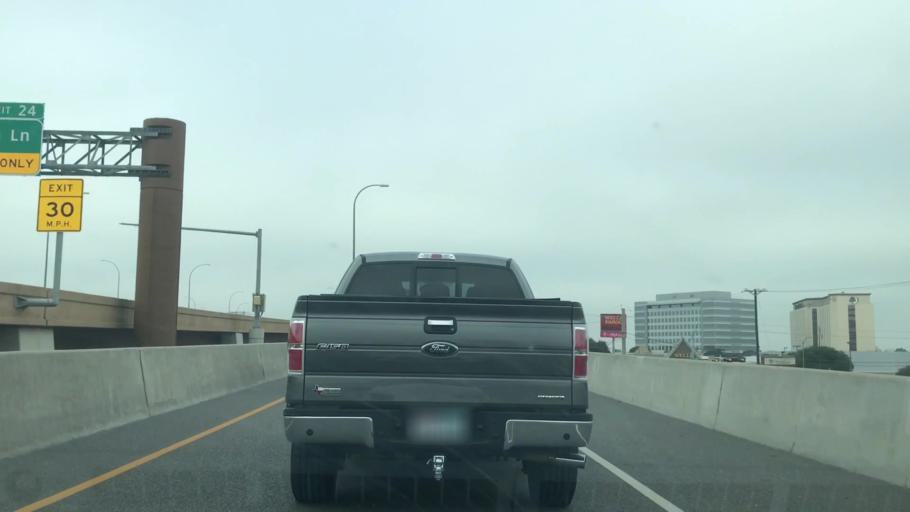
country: US
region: Texas
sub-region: Dallas County
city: Addison
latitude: 32.9258
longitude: -96.8375
